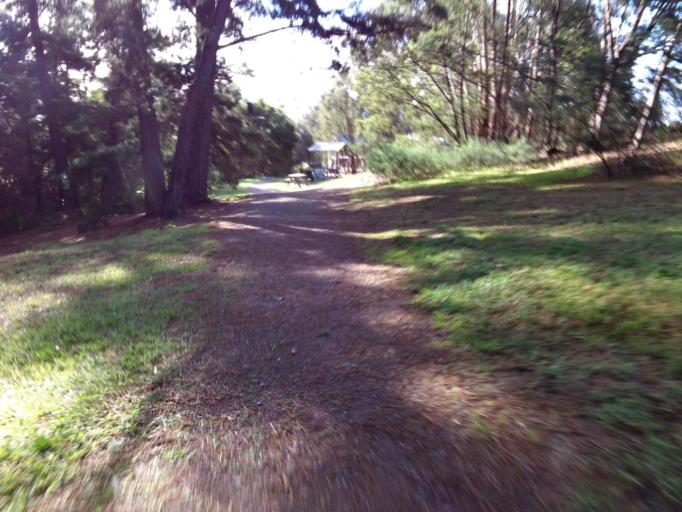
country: AU
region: Victoria
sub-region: Maroondah
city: Croydon Hills
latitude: -37.7747
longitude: 145.2701
